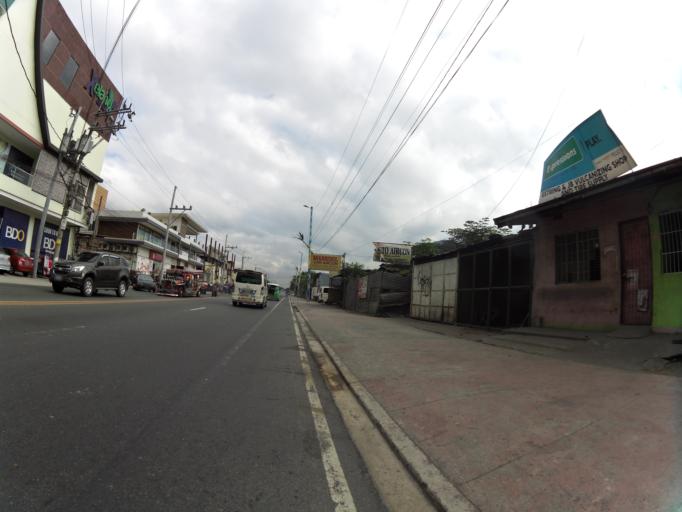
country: PH
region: Metro Manila
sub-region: Marikina
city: Calumpang
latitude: 14.6369
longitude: 121.1019
